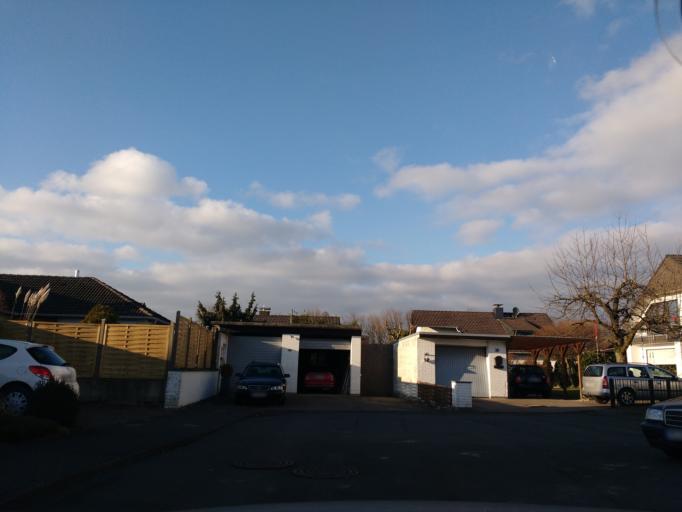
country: DE
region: North Rhine-Westphalia
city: Bad Lippspringe
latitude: 51.7499
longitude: 8.8476
